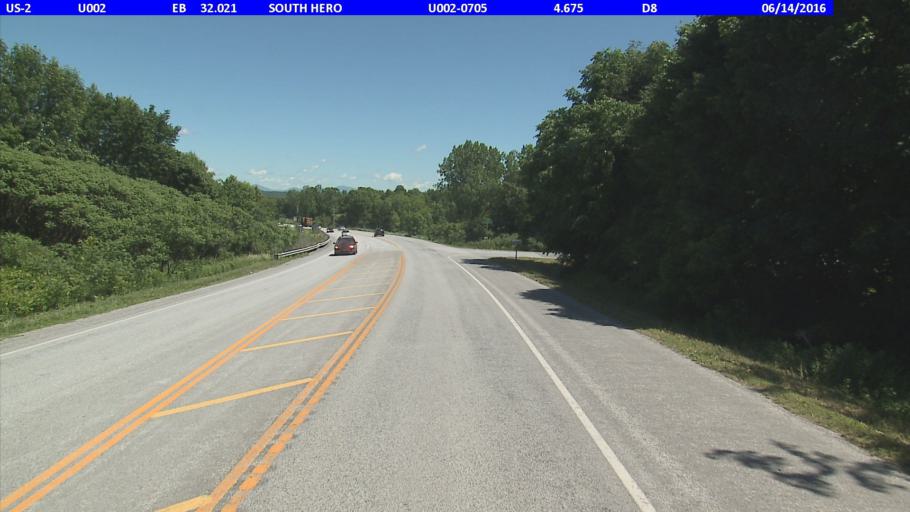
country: US
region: New York
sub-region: Clinton County
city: Cumberland Head
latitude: 44.6390
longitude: -73.2756
